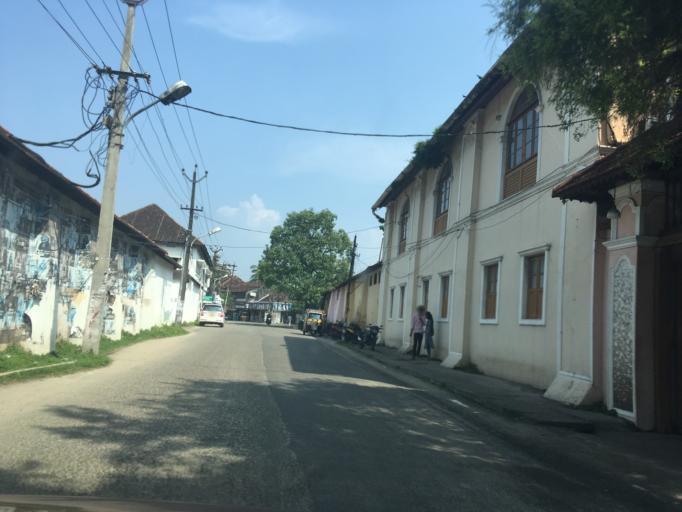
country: IN
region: Kerala
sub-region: Ernakulam
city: Cochin
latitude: 9.9680
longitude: 76.2460
